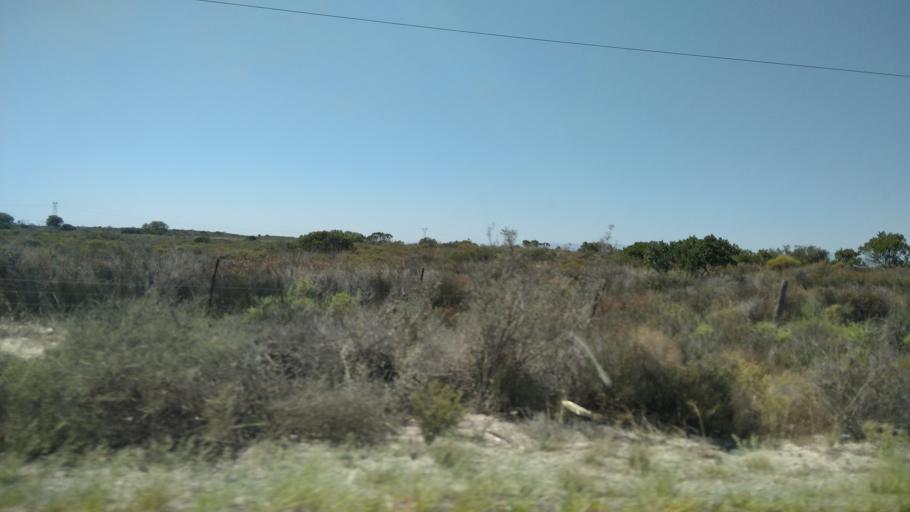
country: ZA
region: Western Cape
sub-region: West Coast District Municipality
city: Vredenburg
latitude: -33.0127
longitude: 18.2396
